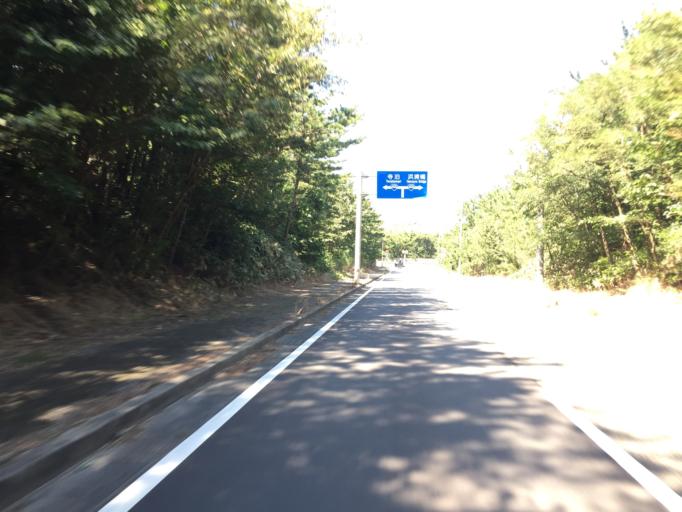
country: JP
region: Niigata
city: Niigata-shi
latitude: 37.9010
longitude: 138.9924
